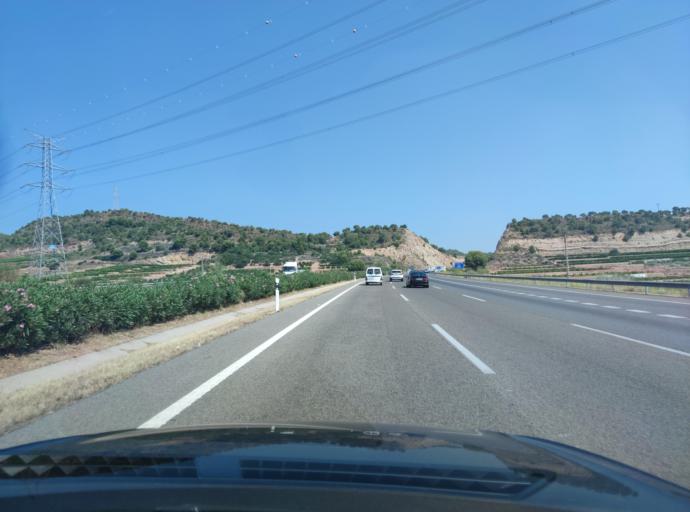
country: ES
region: Valencia
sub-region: Provincia de Valencia
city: Petres
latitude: 39.6556
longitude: -0.3048
